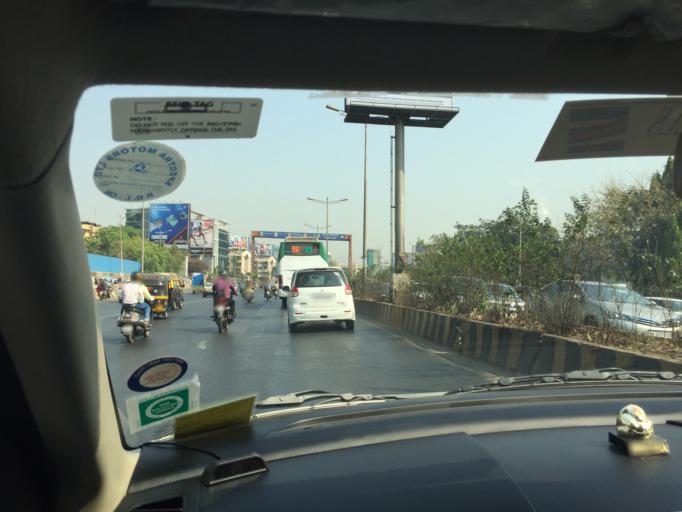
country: IN
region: Maharashtra
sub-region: Mumbai Suburban
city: Mumbai
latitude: 19.1051
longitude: 72.8538
